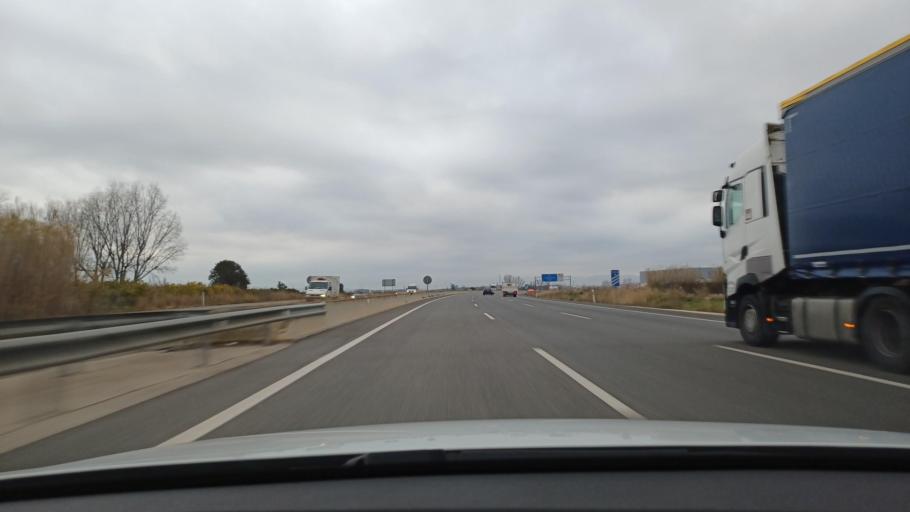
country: ES
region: Valencia
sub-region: Provincia de Valencia
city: Masalaves
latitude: 39.1401
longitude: -0.5264
